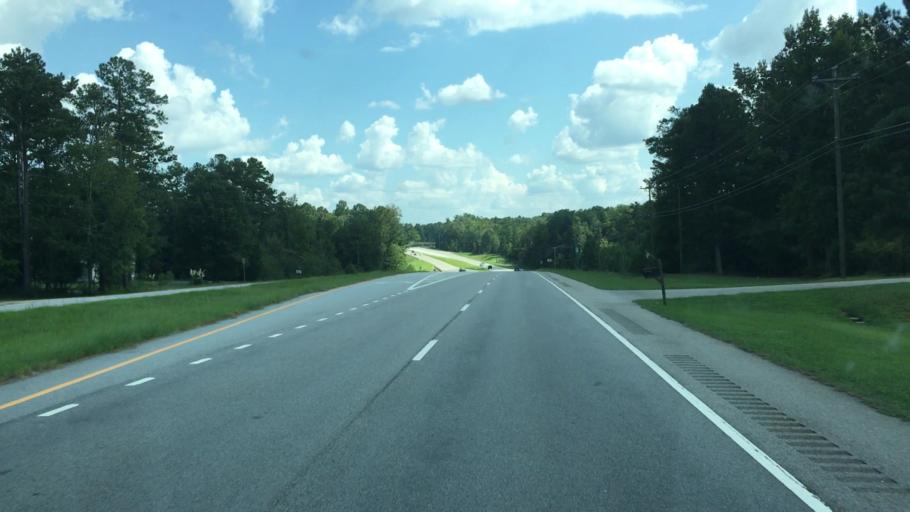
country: US
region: Georgia
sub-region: Putnam County
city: Eatonton
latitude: 33.2447
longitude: -83.3242
